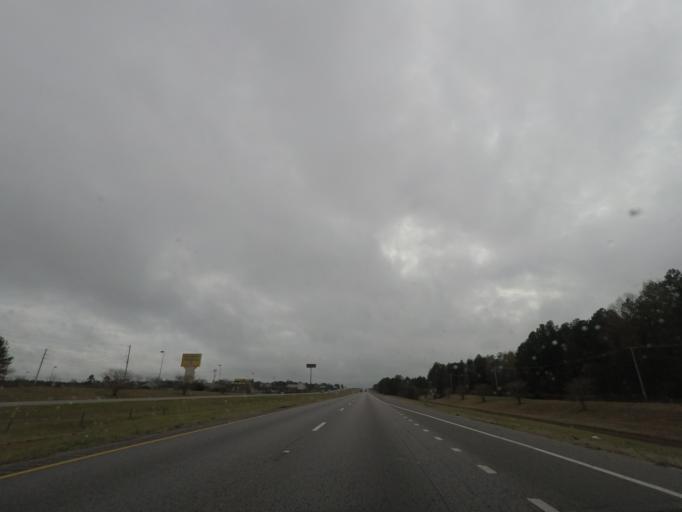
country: US
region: South Carolina
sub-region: Orangeburg County
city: Holly Hill
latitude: 33.4801
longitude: -80.4734
